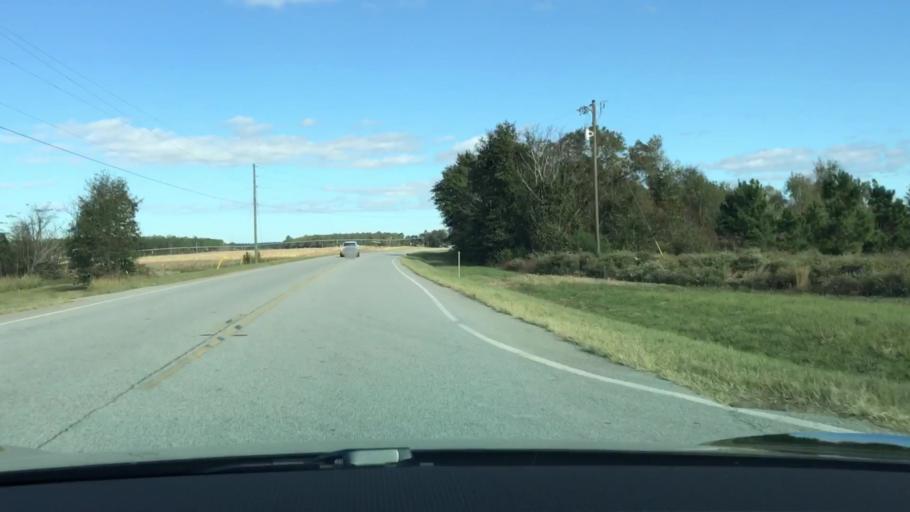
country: US
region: Georgia
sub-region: Jefferson County
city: Wrens
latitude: 33.1491
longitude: -82.4573
